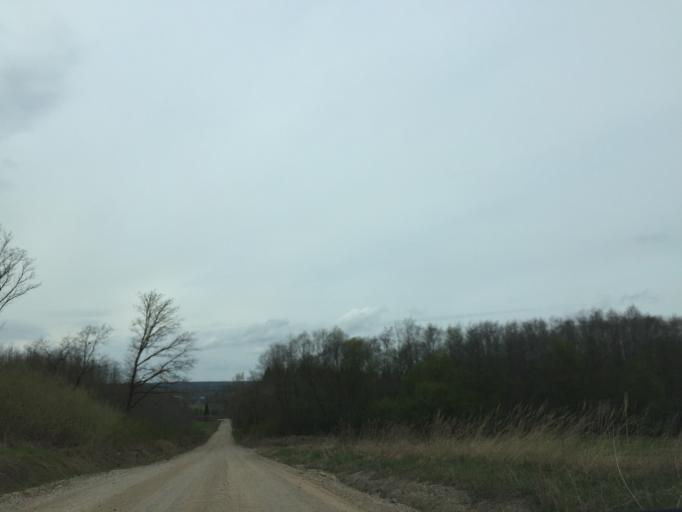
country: LV
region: Priekuli
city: Priekuli
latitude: 57.3432
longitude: 25.3501
